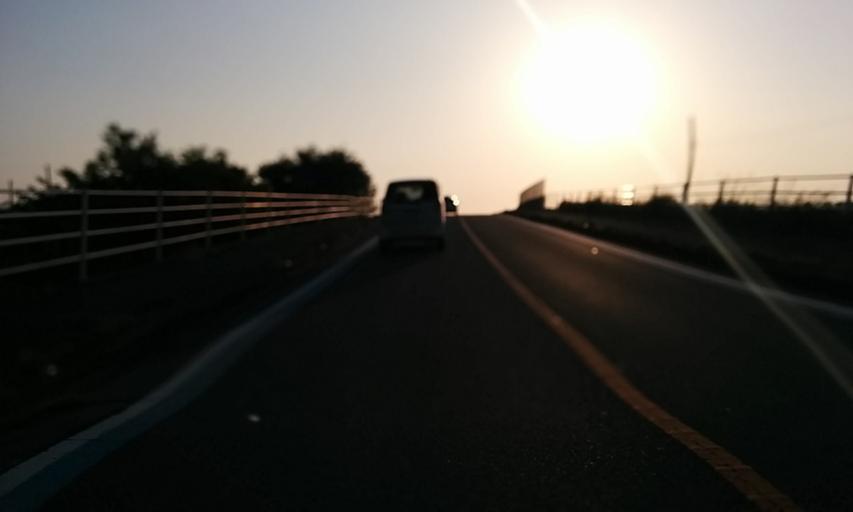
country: JP
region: Ehime
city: Masaki-cho
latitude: 33.7715
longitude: 132.7249
